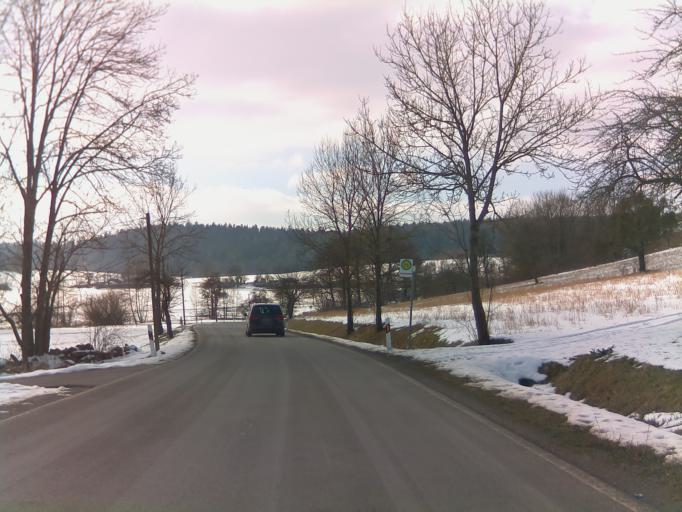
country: DE
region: Thuringia
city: Aschenhausen
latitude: 50.5695
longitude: 10.1975
